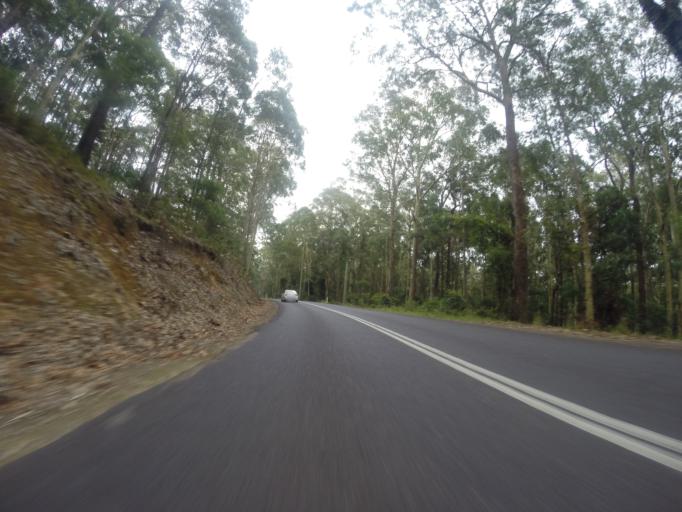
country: AU
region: New South Wales
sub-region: Eurobodalla
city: Batemans Bay
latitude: -35.6617
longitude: 150.2591
